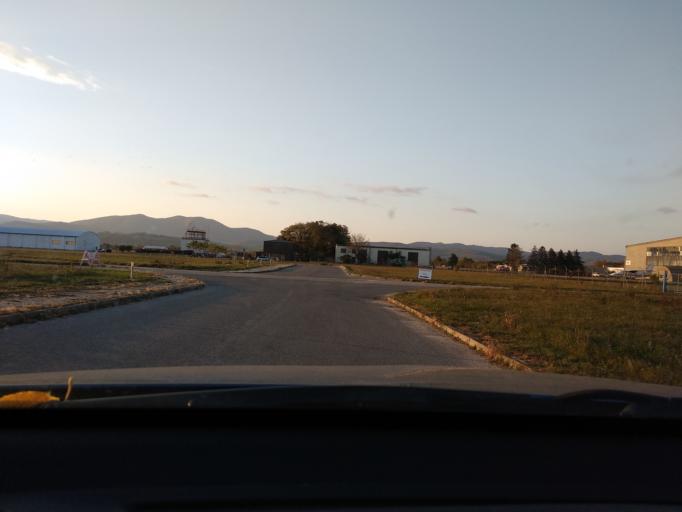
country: SK
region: Trenciansky
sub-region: Okres Trencin
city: Trencin
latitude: 48.8704
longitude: 18.0179
